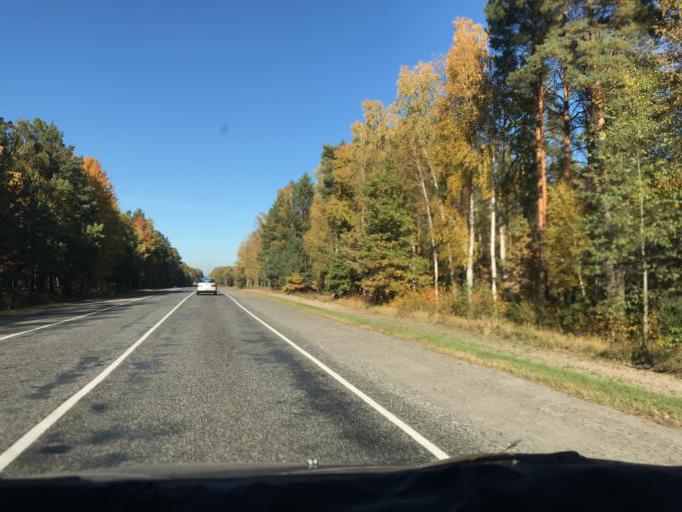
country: BY
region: Gomel
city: Yel'sk
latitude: 51.8476
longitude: 29.2224
